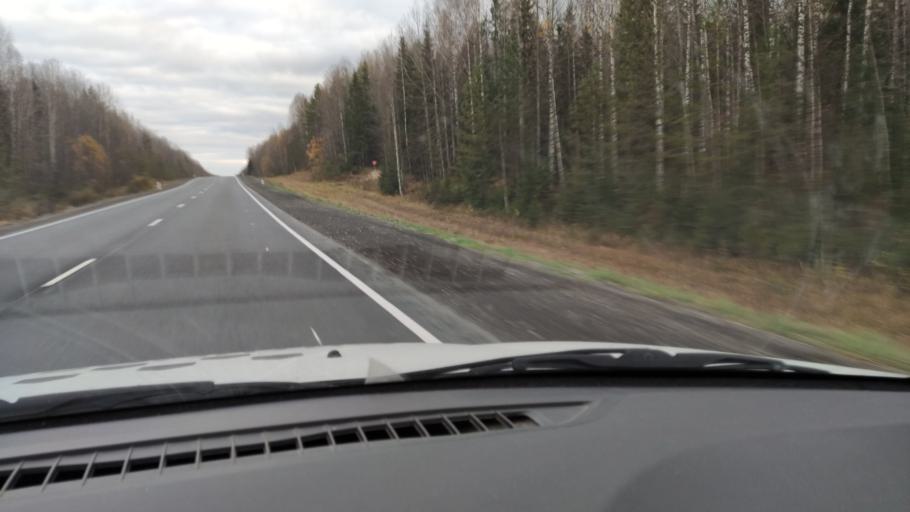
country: RU
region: Kirov
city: Chernaya Kholunitsa
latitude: 58.8824
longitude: 51.4232
